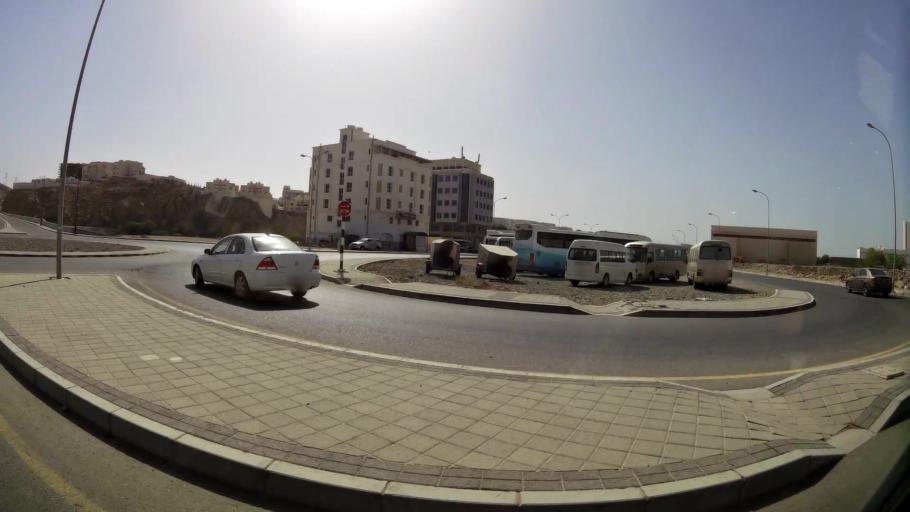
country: OM
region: Muhafazat Masqat
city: Muscat
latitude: 23.6040
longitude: 58.5003
